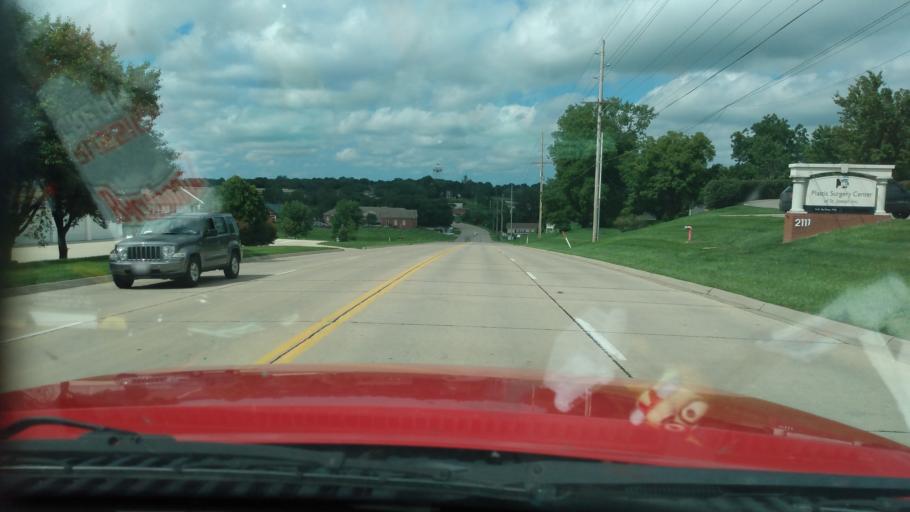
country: US
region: Missouri
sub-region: Andrew County
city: Country Club Village
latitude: 39.7862
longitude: -94.7967
